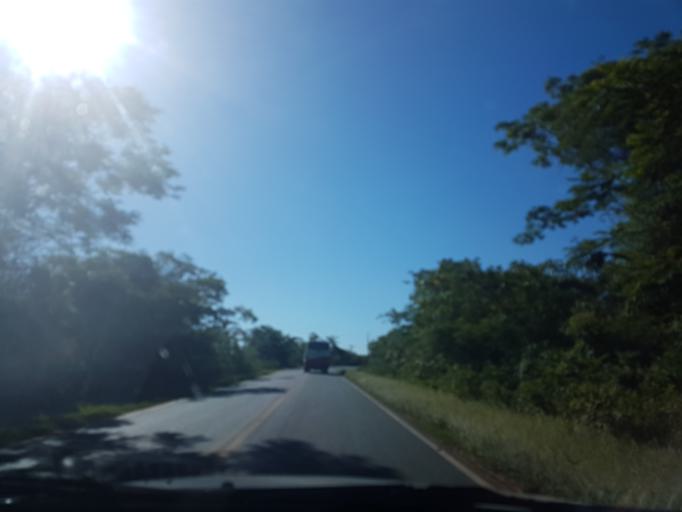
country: PY
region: Cordillera
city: Arroyos y Esteros
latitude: -25.1456
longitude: -57.1076
